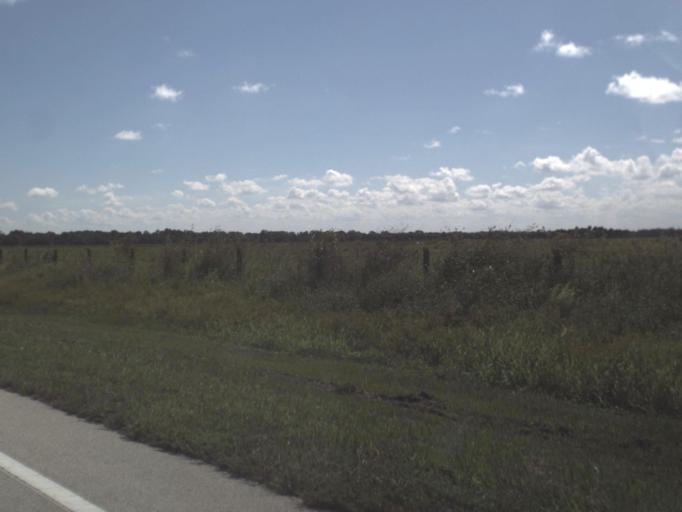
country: US
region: Florida
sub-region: Hendry County
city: Port LaBelle
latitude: 26.8123
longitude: -81.3784
